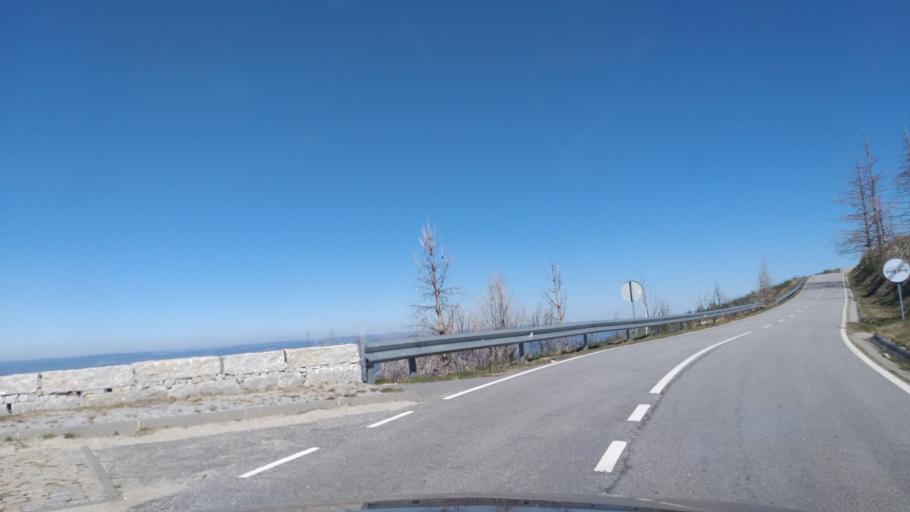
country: PT
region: Guarda
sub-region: Manteigas
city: Manteigas
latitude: 40.4920
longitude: -7.5493
